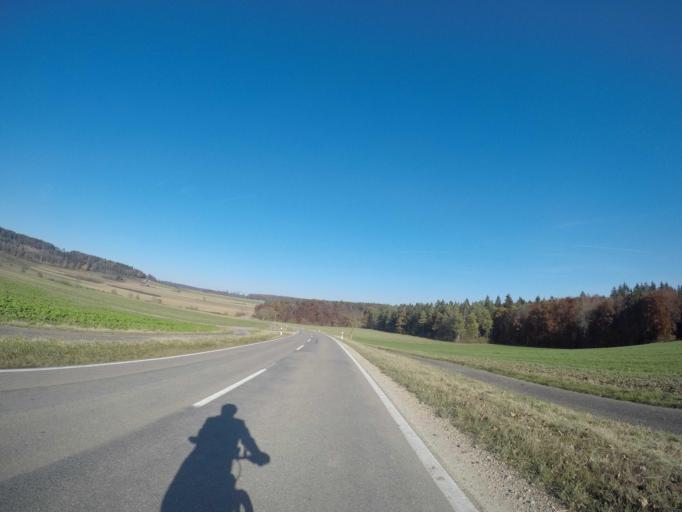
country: DE
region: Baden-Wuerttemberg
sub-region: Tuebingen Region
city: Emeringen
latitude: 48.2421
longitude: 9.5220
